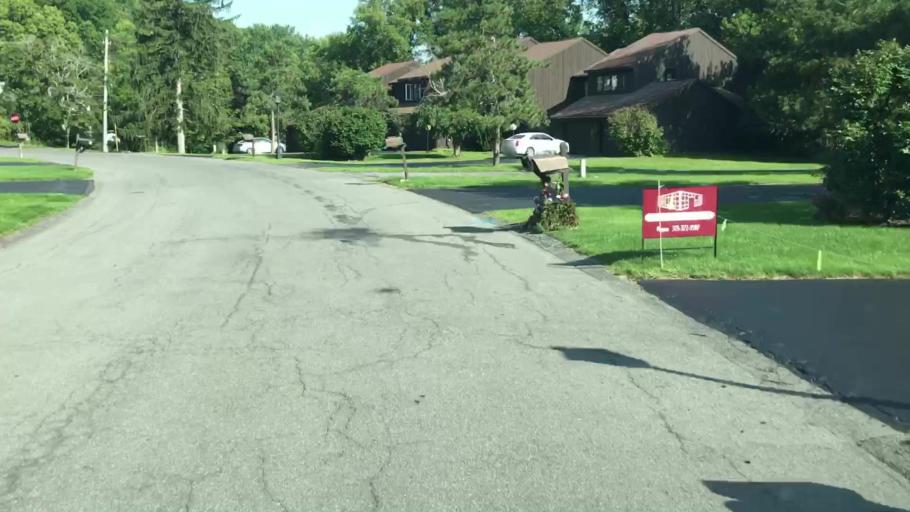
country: US
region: New York
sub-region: Onondaga County
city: Manlius
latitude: 42.9926
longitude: -75.9913
